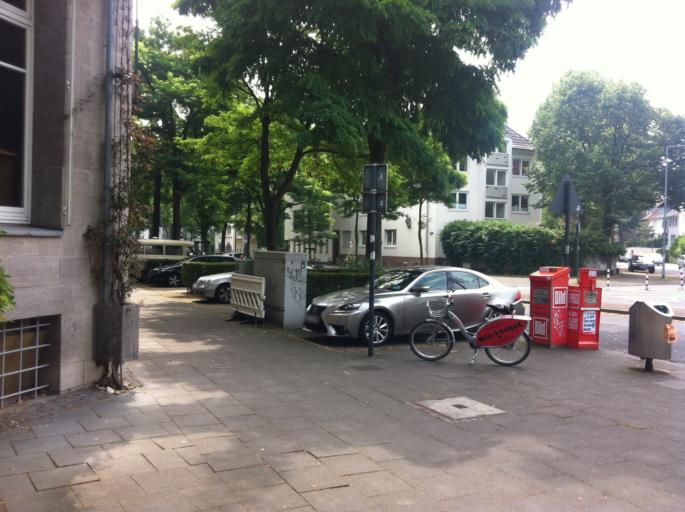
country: DE
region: North Rhine-Westphalia
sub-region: Regierungsbezirk Koln
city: Altstadt Nord
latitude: 50.9531
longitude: 6.9654
